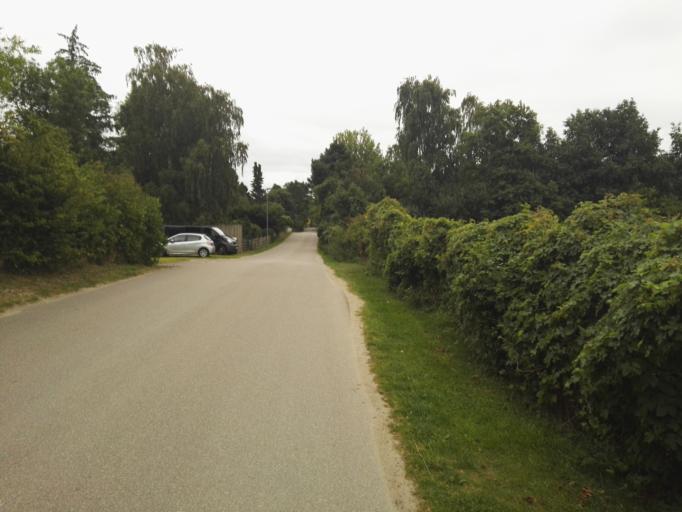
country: DK
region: Zealand
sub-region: Odsherred Kommune
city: Nykobing Sjaelland
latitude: 55.9383
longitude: 11.6639
